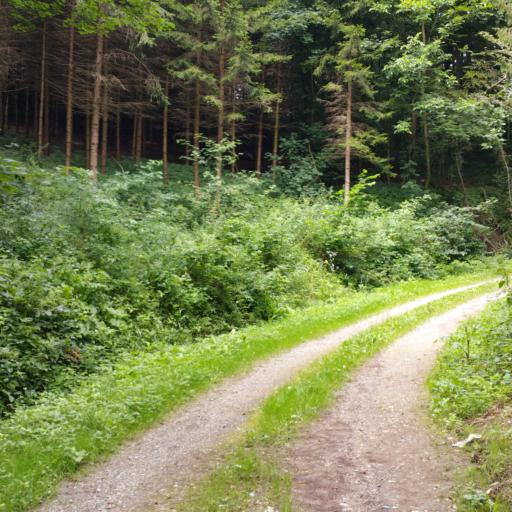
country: AT
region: Styria
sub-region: Politischer Bezirk Leibnitz
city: Gleinstatten
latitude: 46.7426
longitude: 15.3697
